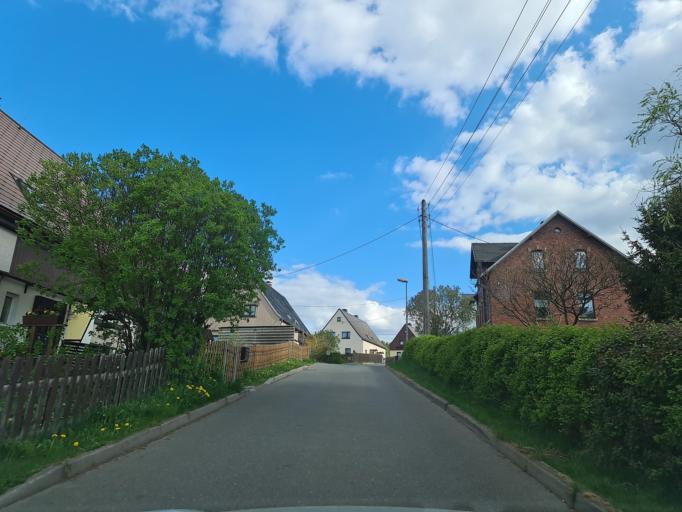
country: DE
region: Saxony
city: Ellefeld
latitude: 50.4699
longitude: 12.3900
